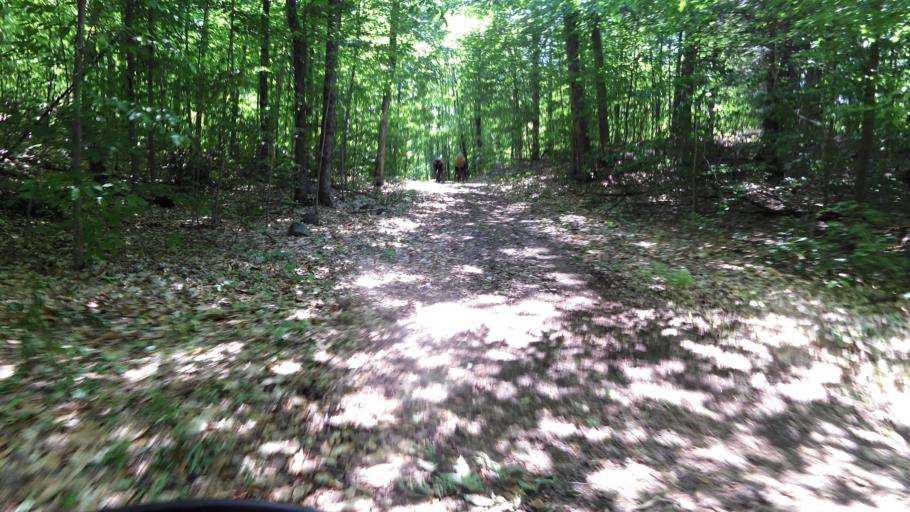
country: CA
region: Quebec
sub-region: Outaouais
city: Wakefield
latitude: 45.5957
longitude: -75.9676
